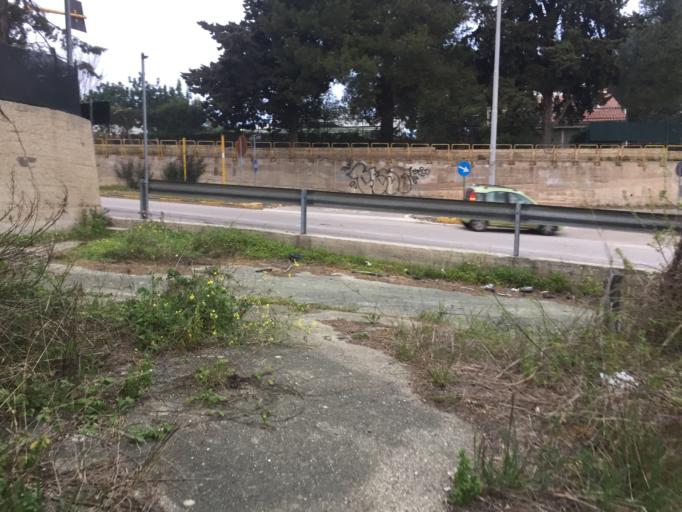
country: IT
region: Apulia
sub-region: Provincia di Bari
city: Parco Scizzo-Parchitello
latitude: 41.0811
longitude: 16.9972
